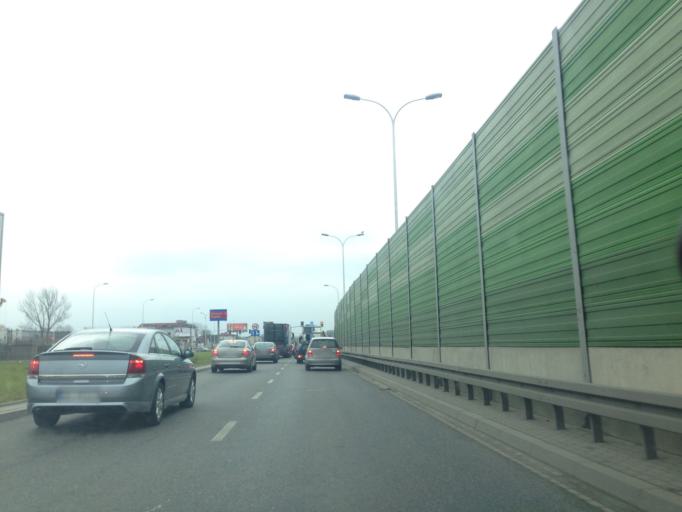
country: PL
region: Masovian Voivodeship
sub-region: Warszawa
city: Rembertow
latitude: 52.2432
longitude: 21.1373
